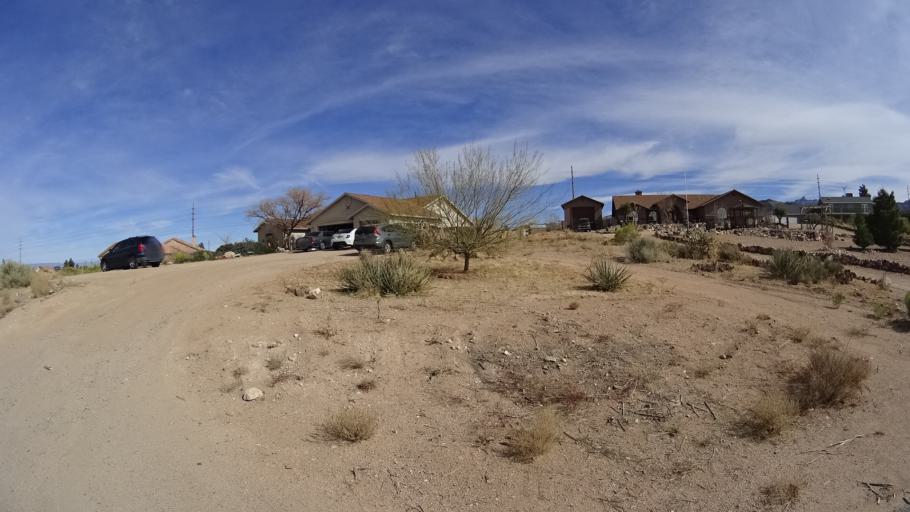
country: US
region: Arizona
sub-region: Mohave County
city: Kingman
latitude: 35.1831
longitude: -113.9845
